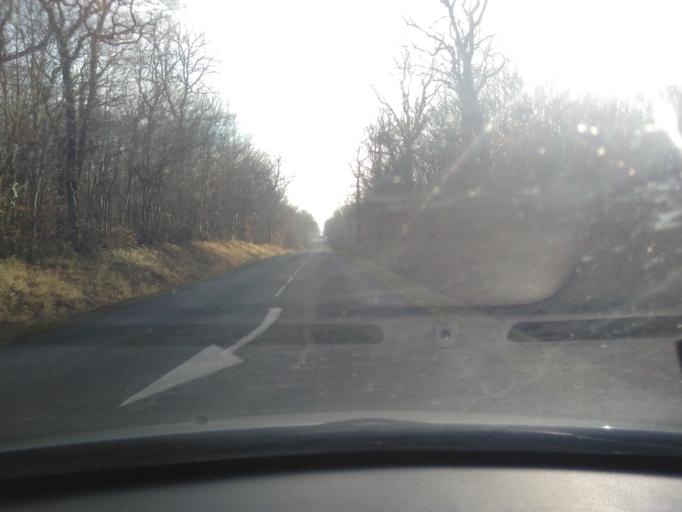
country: FR
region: Bourgogne
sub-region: Departement de la Nievre
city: Saint-Parize-le-Chatel
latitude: 46.8088
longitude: 3.2651
